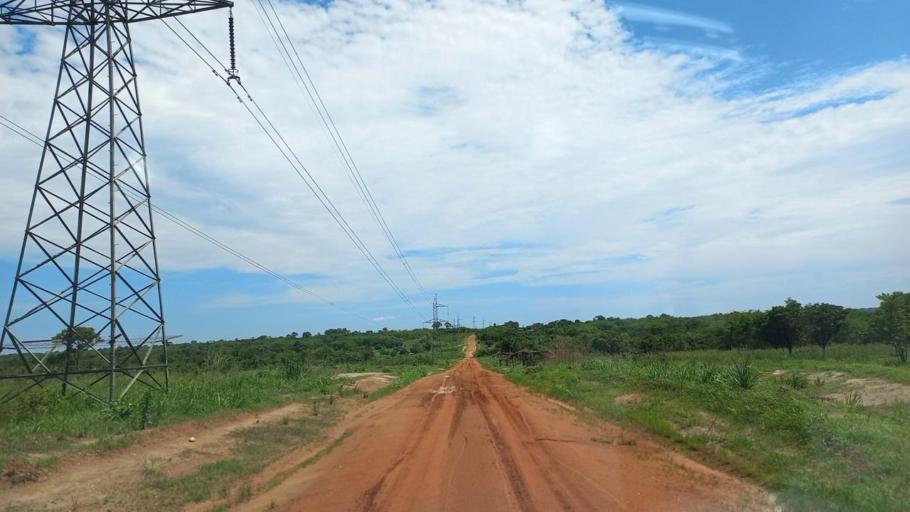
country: ZM
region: Copperbelt
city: Kitwe
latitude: -12.8323
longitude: 28.3450
